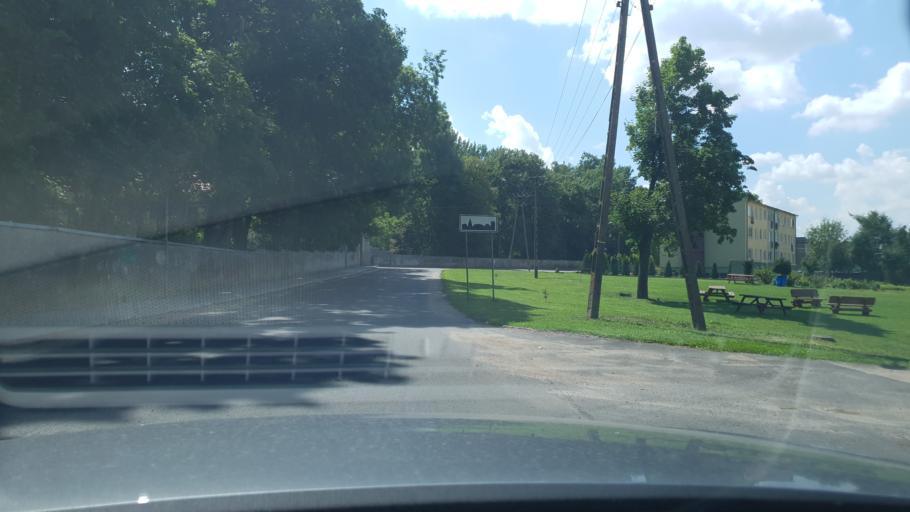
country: PL
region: Kujawsko-Pomorskie
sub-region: Powiat wabrzeski
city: Pluznica
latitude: 53.3478
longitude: 18.8320
